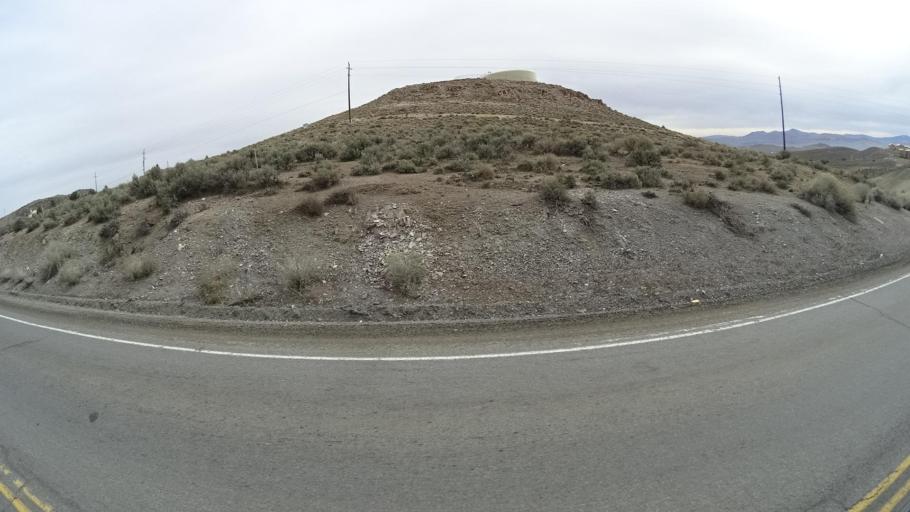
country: US
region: Nevada
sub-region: Washoe County
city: Golden Valley
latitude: 39.6027
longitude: -119.8089
